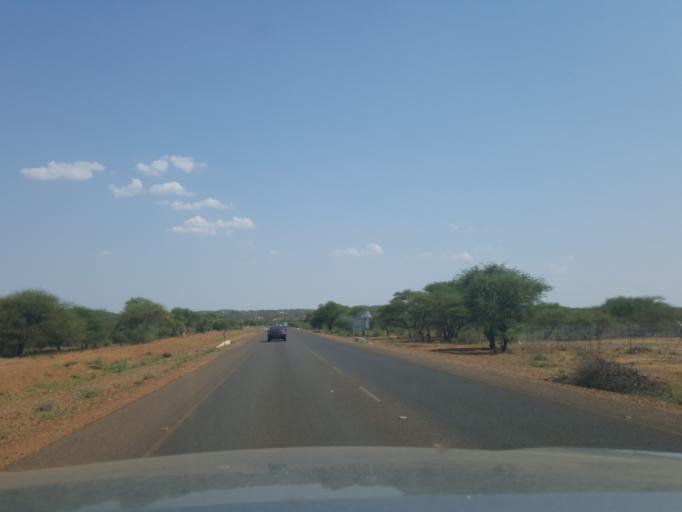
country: BW
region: South East
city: Ramotswa
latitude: -24.8549
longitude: 25.8291
